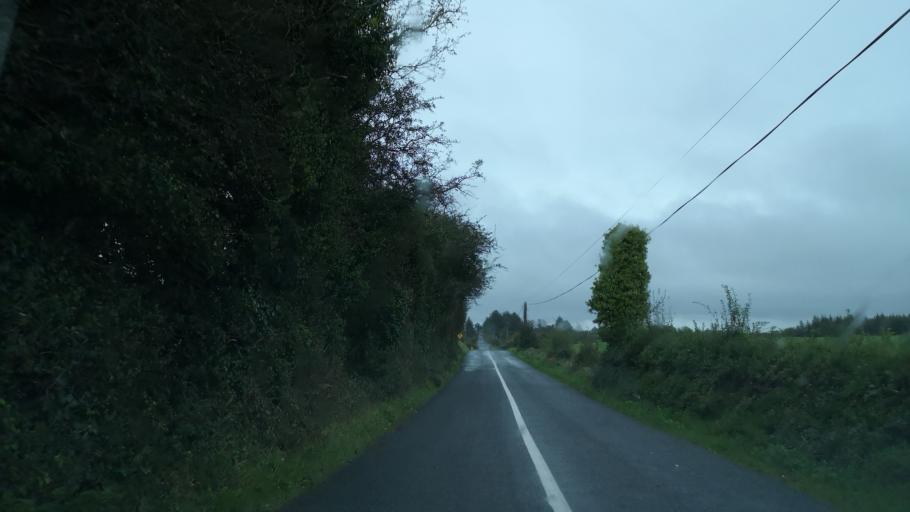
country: IE
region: Connaught
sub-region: Maigh Eo
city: Ballyhaunis
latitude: 53.7814
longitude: -8.7338
